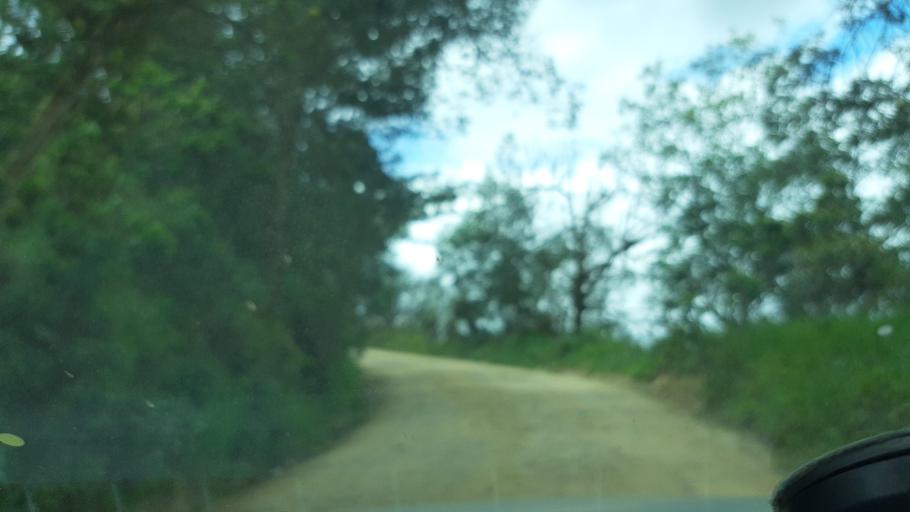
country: CO
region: Cundinamarca
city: Umbita
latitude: 5.2190
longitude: -73.4422
